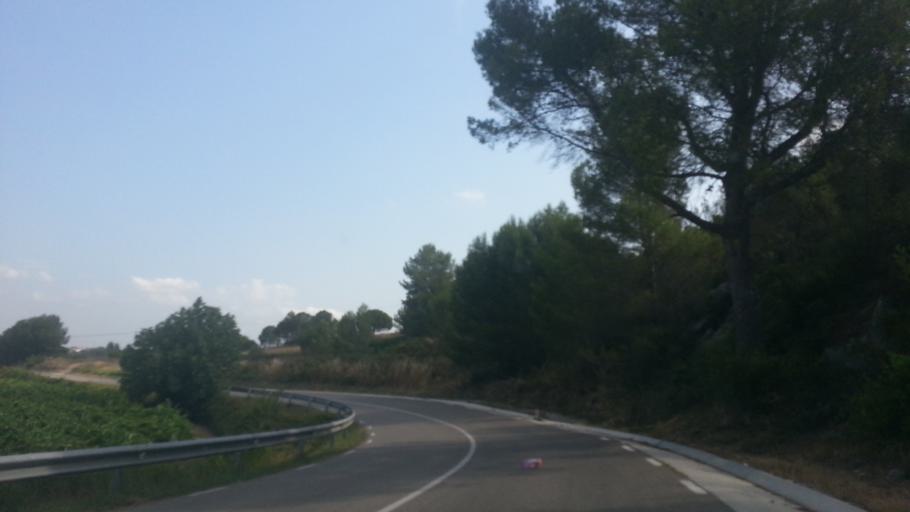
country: ES
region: Catalonia
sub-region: Provincia de Barcelona
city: Avinyonet del Penedes
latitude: 41.3342
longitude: 1.7499
